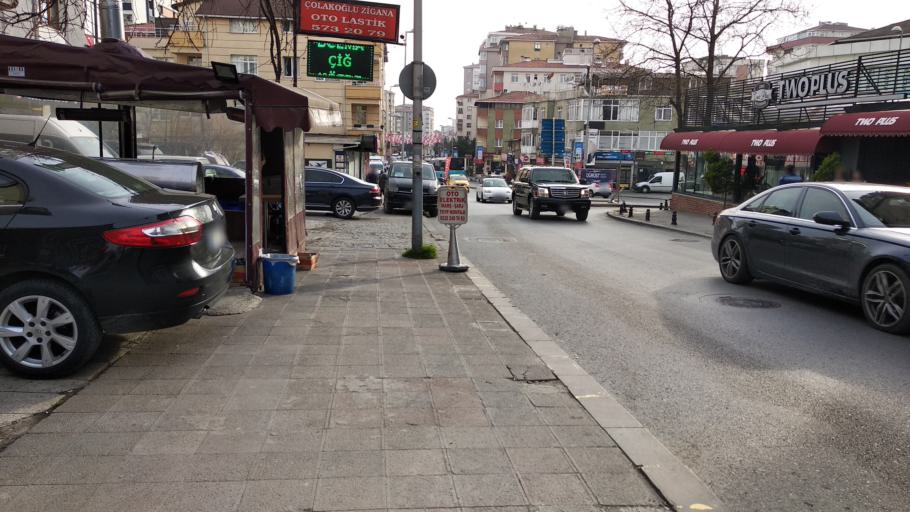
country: TR
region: Istanbul
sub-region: Atasehir
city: Atasehir
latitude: 40.9778
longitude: 29.1139
